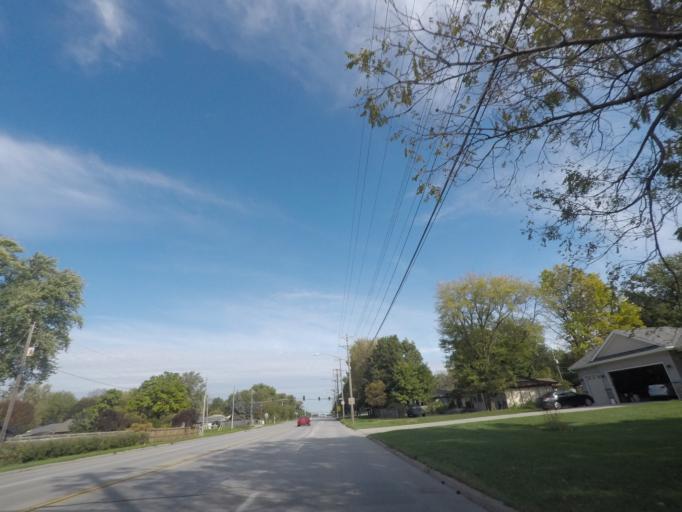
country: US
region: Iowa
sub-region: Story County
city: Ames
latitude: 42.0410
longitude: -93.6204
